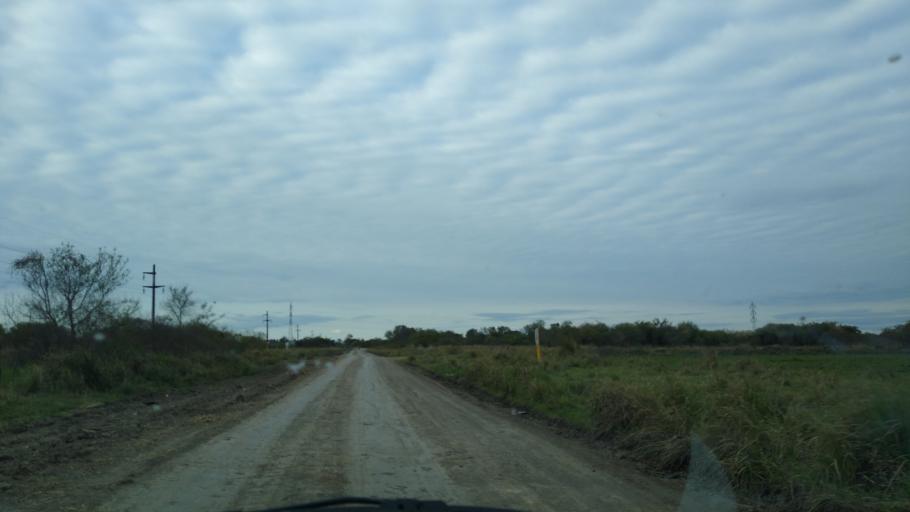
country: AR
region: Chaco
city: Fontana
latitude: -27.3890
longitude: -59.0480
